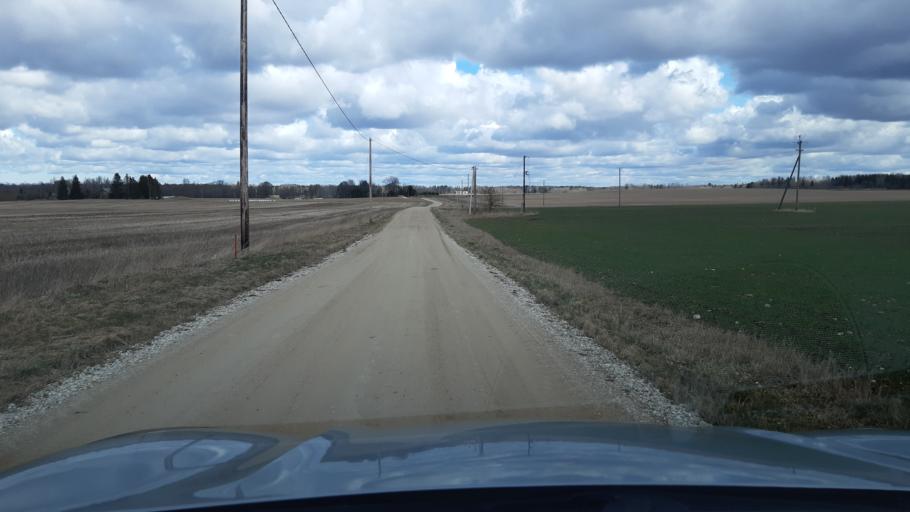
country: EE
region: Harju
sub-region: Rae vald
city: Vaida
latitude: 59.0805
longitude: 25.1240
